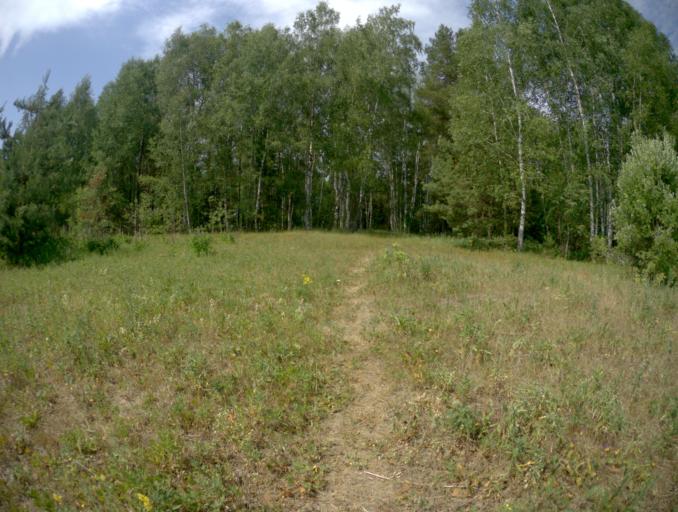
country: RU
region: Vladimir
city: Raduzhnyy
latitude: 56.0220
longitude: 40.2433
